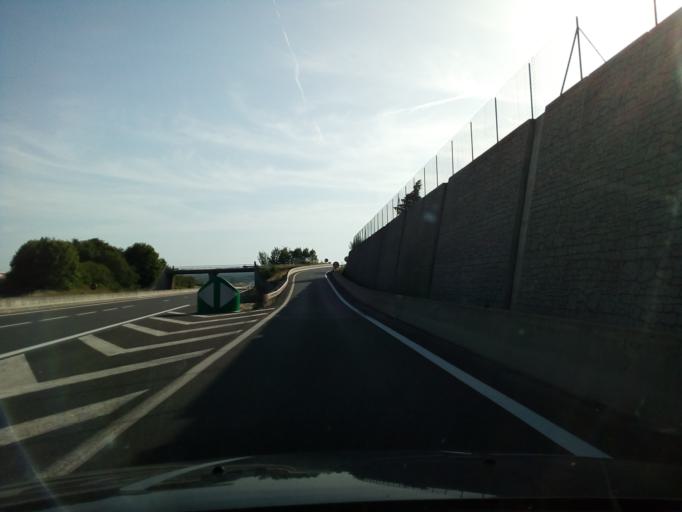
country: FR
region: Auvergne
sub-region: Departement de l'Allier
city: Domerat
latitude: 46.3715
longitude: 2.5695
